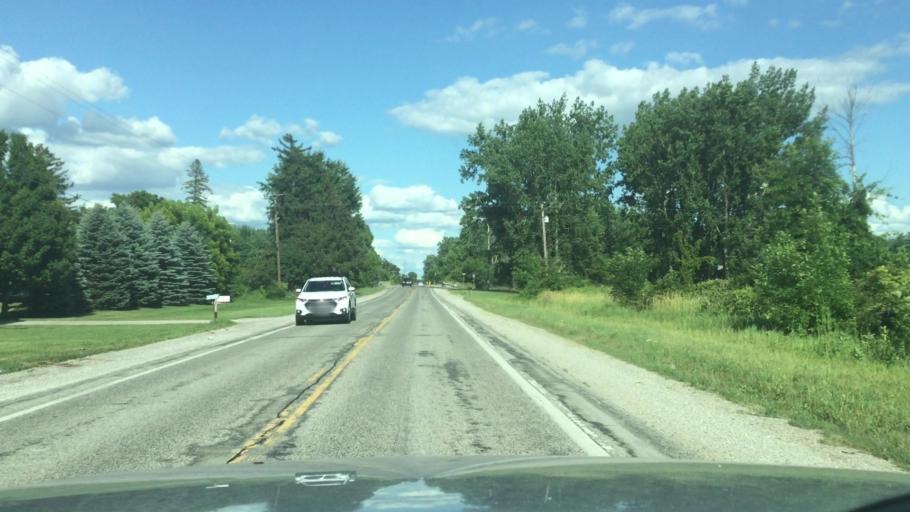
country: US
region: Michigan
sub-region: Saginaw County
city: Shields
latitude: 43.3797
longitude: -84.1027
